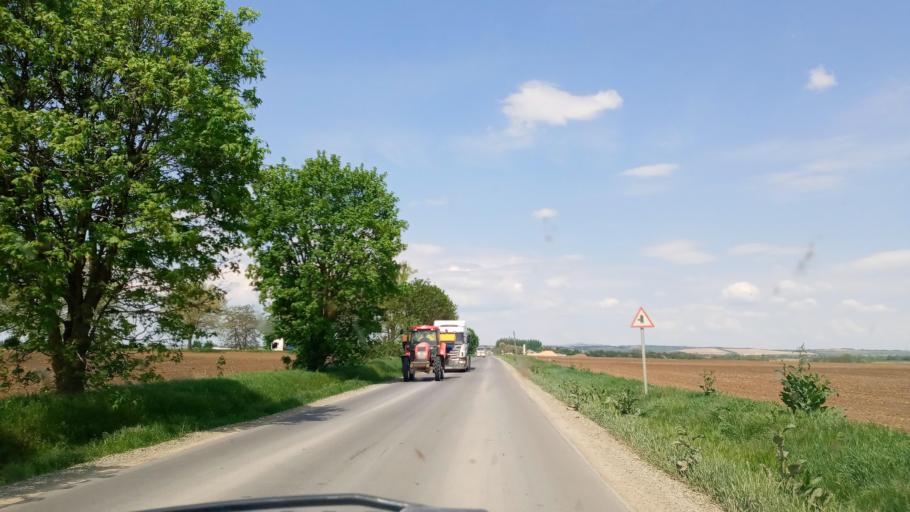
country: HU
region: Baranya
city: Boly
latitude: 45.9466
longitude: 18.5372
